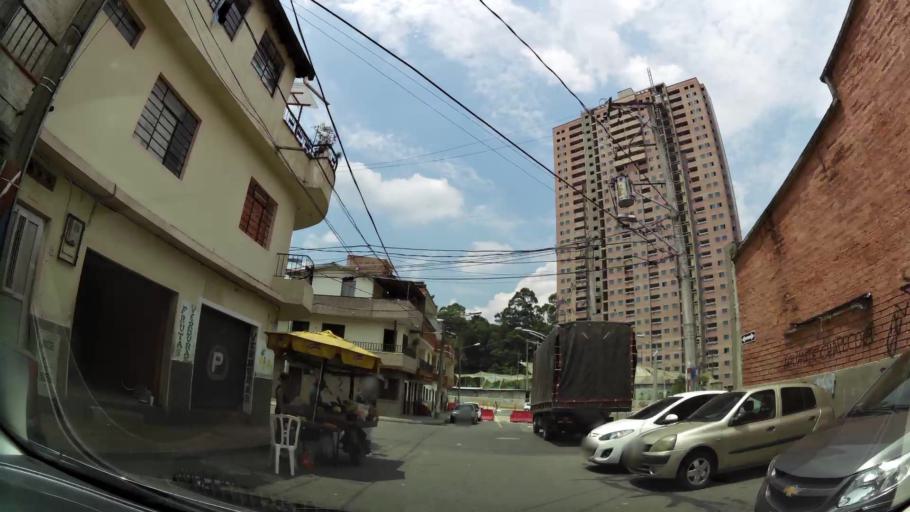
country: CO
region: Antioquia
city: Itagui
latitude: 6.1752
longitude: -75.6080
